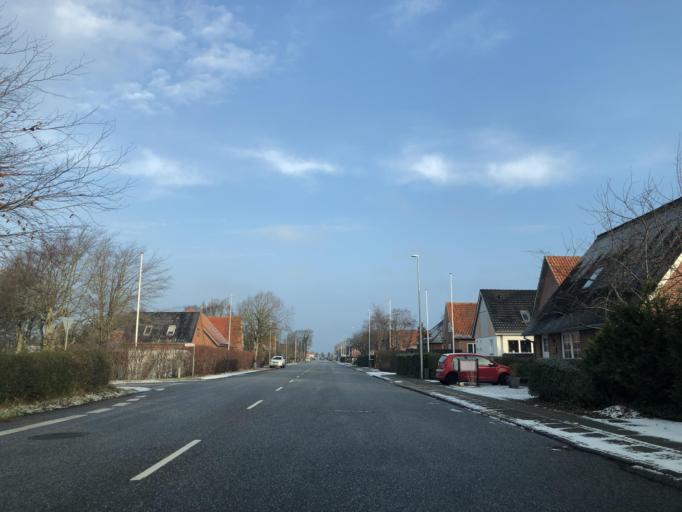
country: DK
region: Central Jutland
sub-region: Ringkobing-Skjern Kommune
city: Tarm
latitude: 55.8993
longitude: 8.5153
